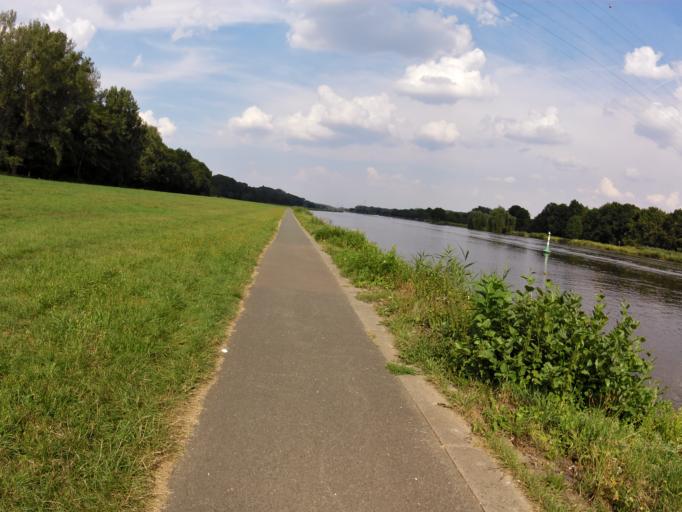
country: DE
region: North Rhine-Westphalia
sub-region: Regierungsbezirk Detmold
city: Minden
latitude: 52.3274
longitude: 8.9277
